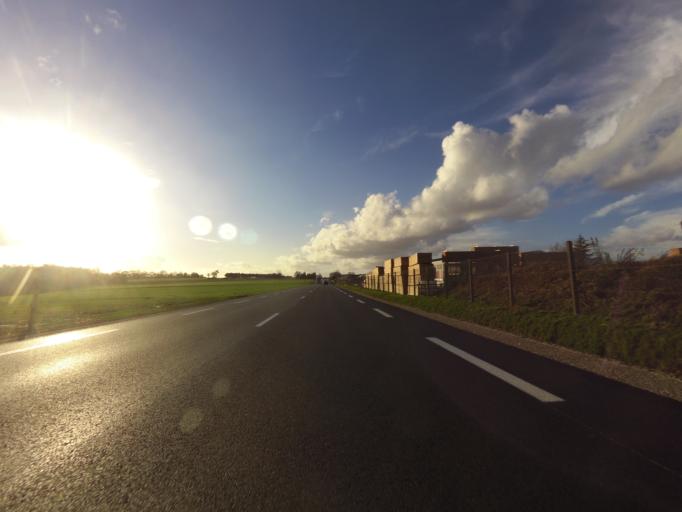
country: FR
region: Brittany
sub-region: Departement du Morbihan
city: Pleugriffet
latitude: 47.9795
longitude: -2.6830
